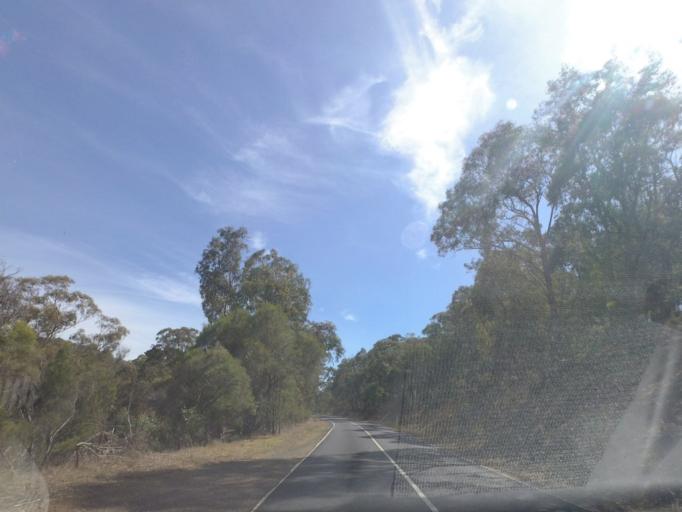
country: AU
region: Victoria
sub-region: Nillumbik
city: Saint Andrews
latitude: -37.6099
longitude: 145.2378
